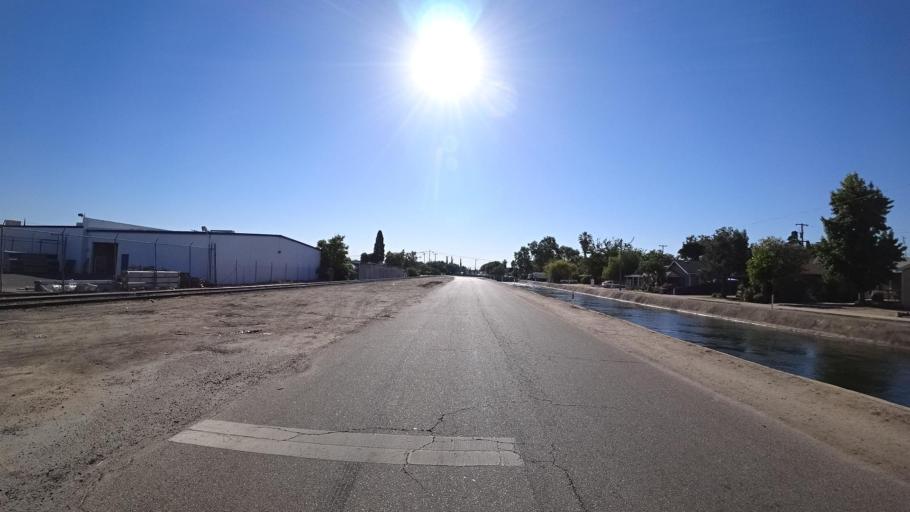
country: US
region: California
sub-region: Fresno County
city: Fresno
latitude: 36.7614
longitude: -119.7854
